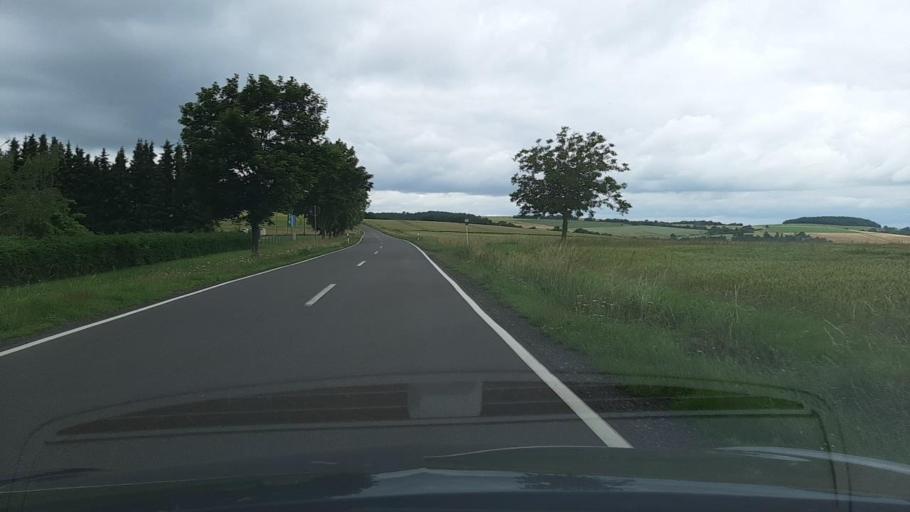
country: DE
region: Rheinland-Pfalz
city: Dommershausen
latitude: 50.1476
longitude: 7.3973
